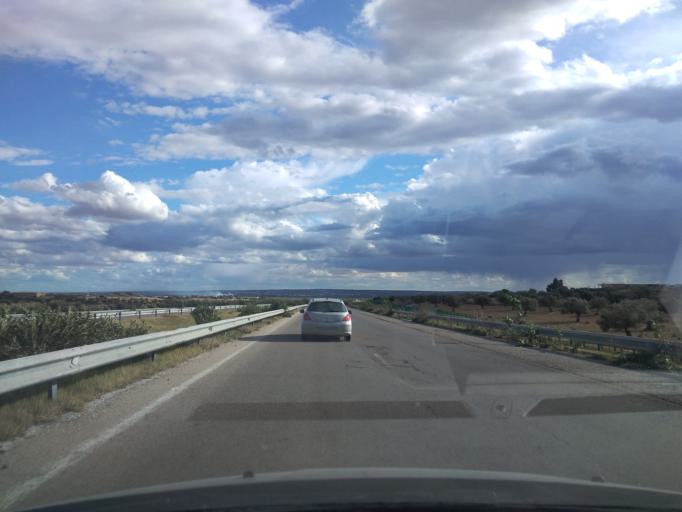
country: TN
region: Al Munastir
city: Manzil Kamil
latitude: 35.5342
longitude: 10.6244
